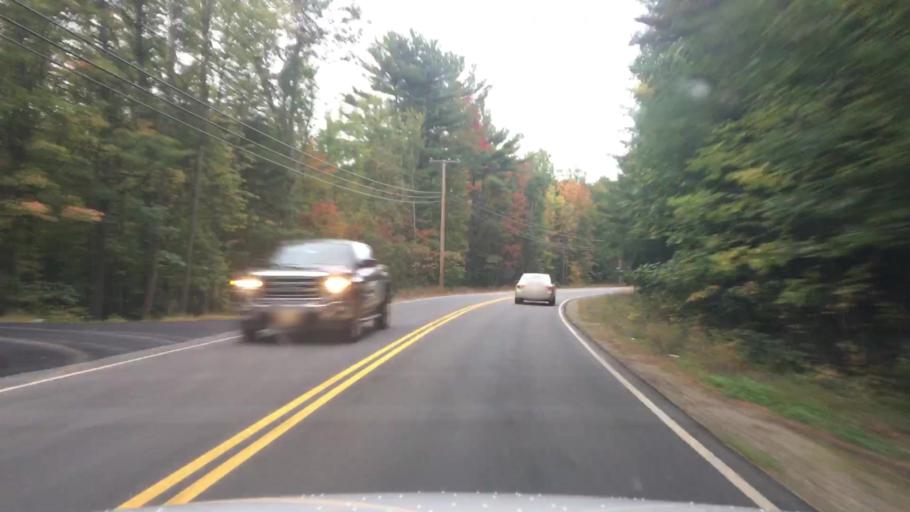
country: US
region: Maine
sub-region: York County
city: Hollis Center
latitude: 43.6106
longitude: -70.5704
